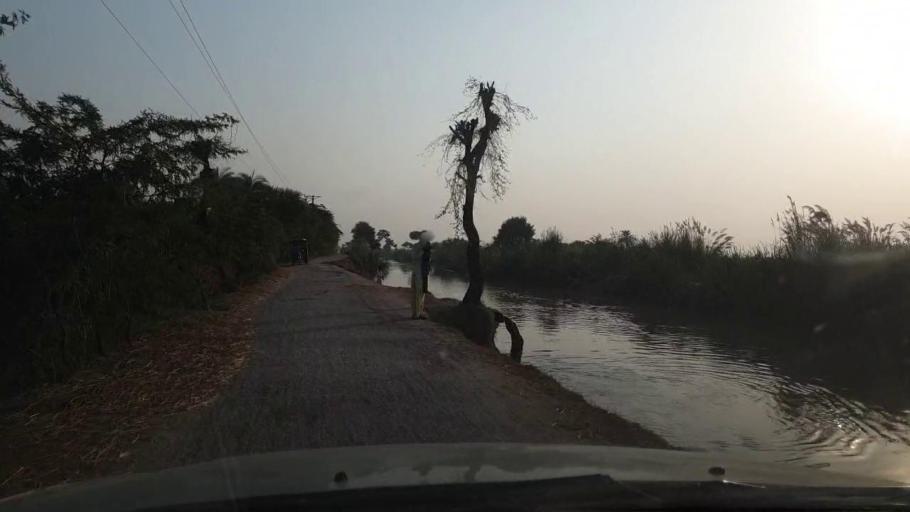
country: PK
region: Sindh
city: Tando Muhammad Khan
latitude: 25.0342
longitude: 68.4348
